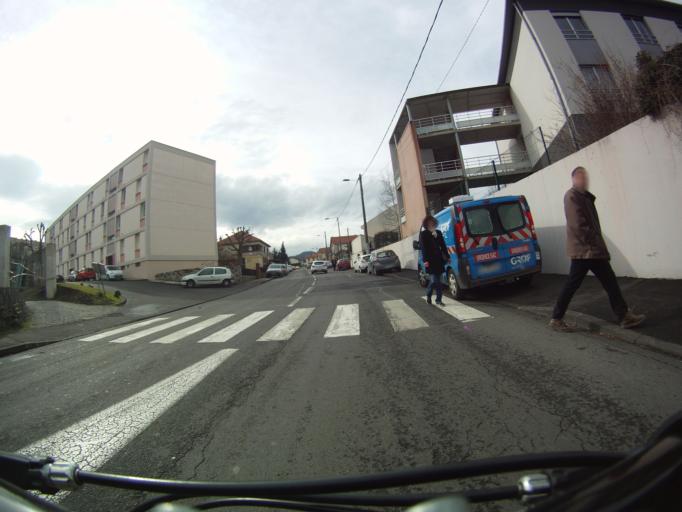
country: FR
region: Auvergne
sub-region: Departement du Puy-de-Dome
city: Aubiere
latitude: 45.7483
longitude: 3.1102
